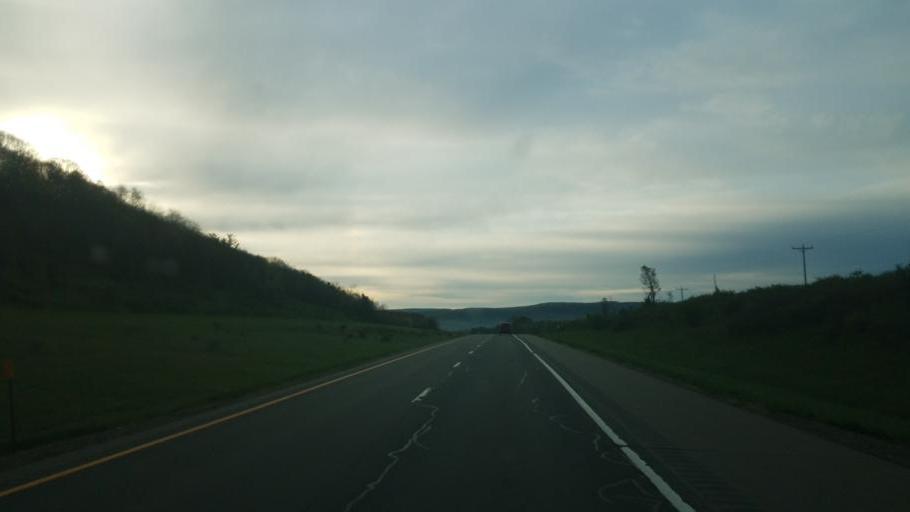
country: US
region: New York
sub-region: Allegany County
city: Friendship
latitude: 42.2056
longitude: -78.1831
